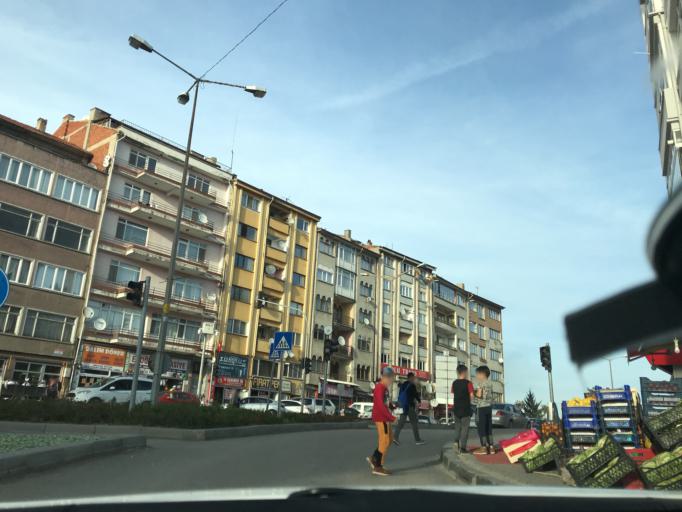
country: TR
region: Bolu
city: Bolu
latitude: 40.7337
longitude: 31.6139
